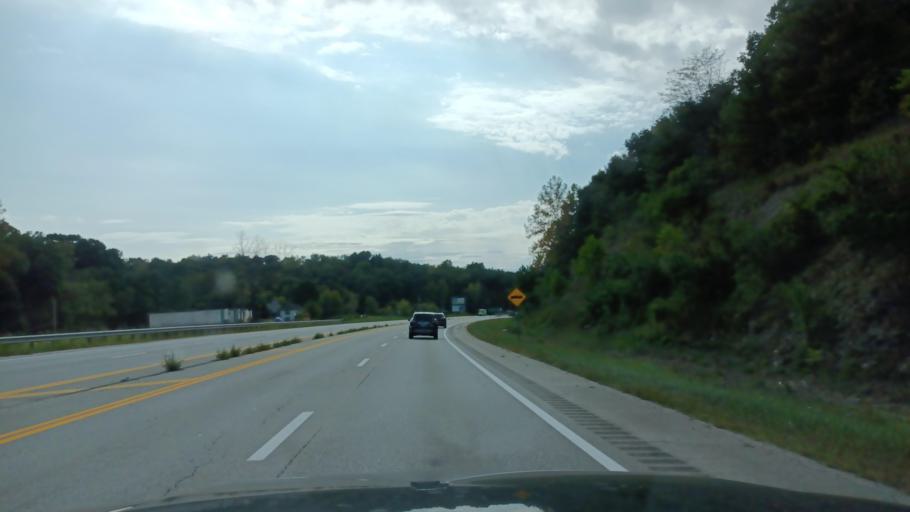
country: US
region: Ohio
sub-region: Athens County
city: Athens
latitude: 39.2918
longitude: -82.1220
